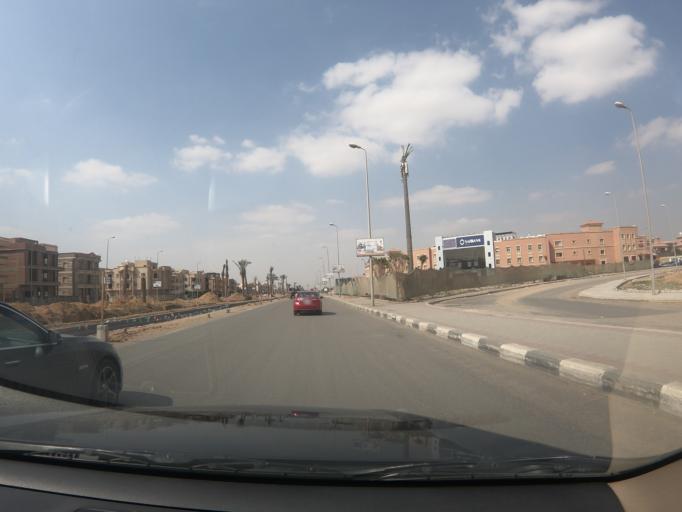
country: EG
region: Muhafazat al Qalyubiyah
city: Al Khankah
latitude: 30.0444
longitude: 31.4752
